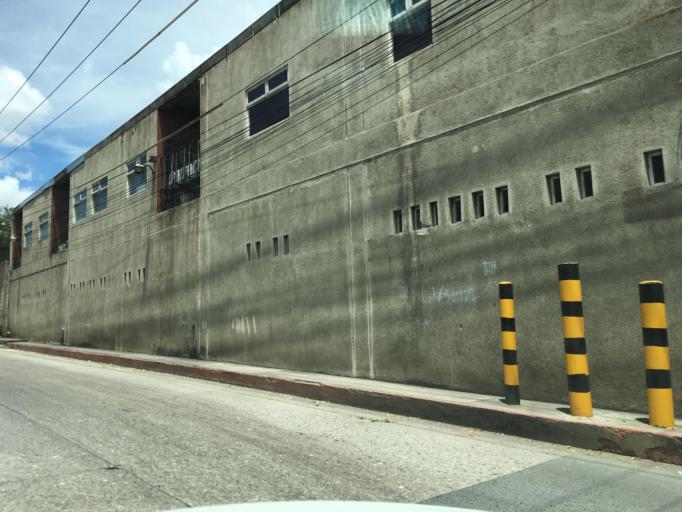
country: GT
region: Guatemala
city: Santa Catarina Pinula
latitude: 14.5865
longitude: -90.5402
